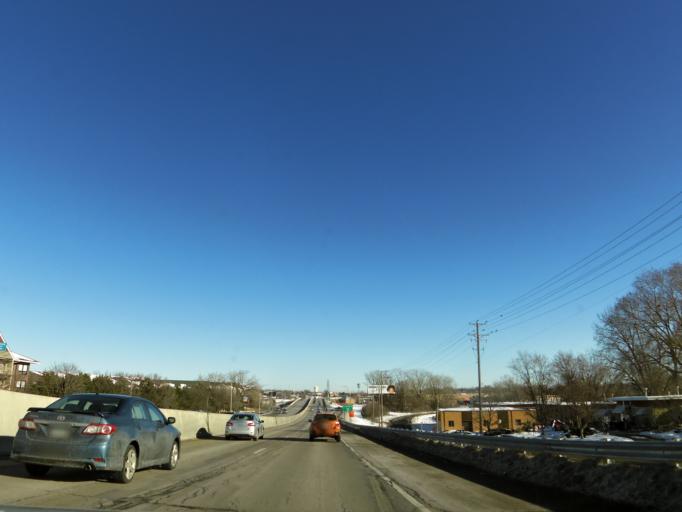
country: US
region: Minnesota
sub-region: Hennepin County
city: Saint Louis Park
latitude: 44.9369
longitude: -93.3762
